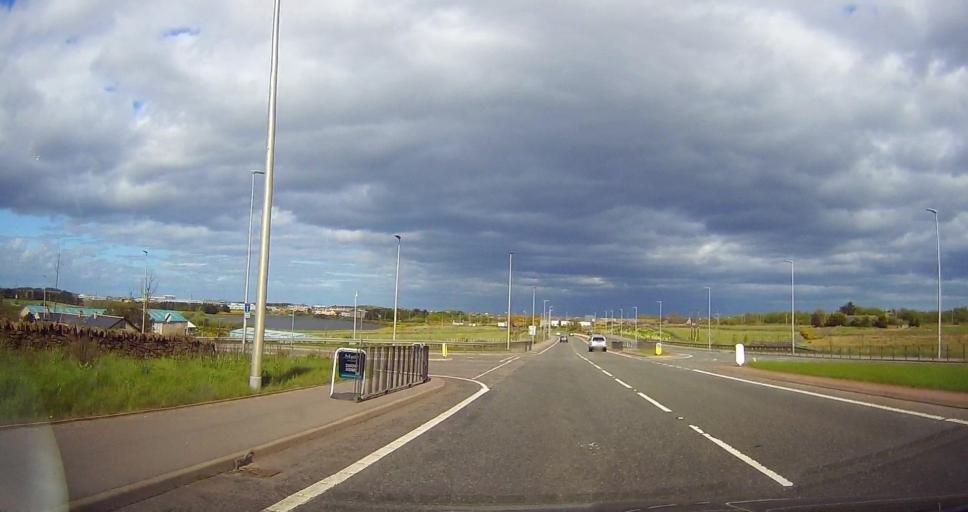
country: GB
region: Scotland
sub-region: Aberdeenshire
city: Portlethen
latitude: 57.0959
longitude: -2.1109
